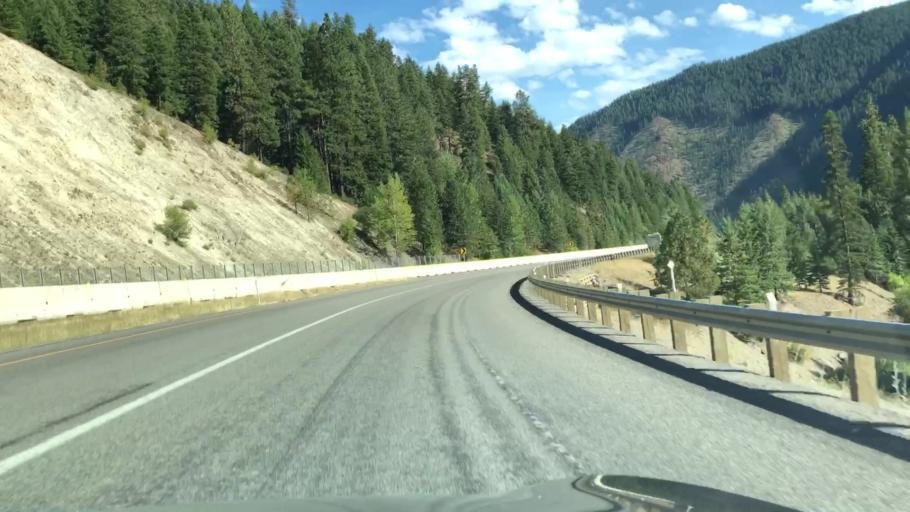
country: US
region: Montana
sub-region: Sanders County
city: Thompson Falls
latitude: 47.3117
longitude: -115.2104
